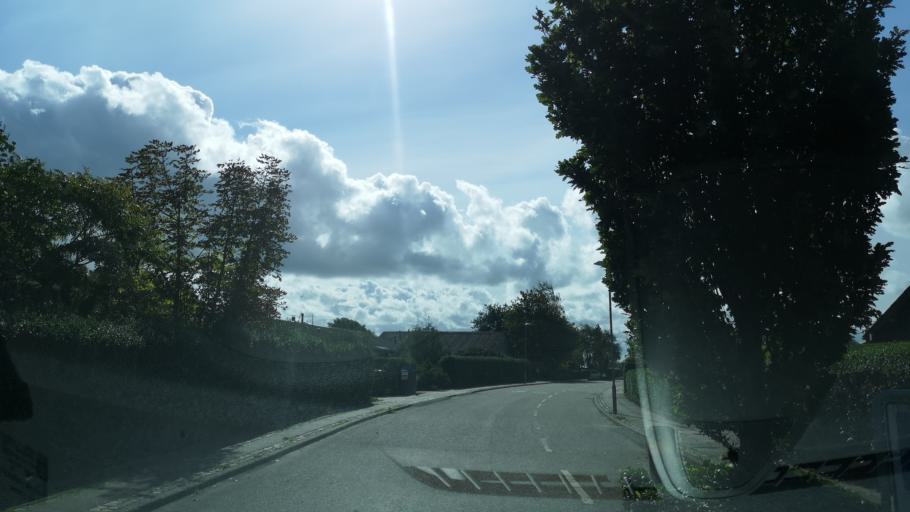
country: DK
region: Central Jutland
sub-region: Ringkobing-Skjern Kommune
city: Skjern
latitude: 55.9840
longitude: 8.5442
